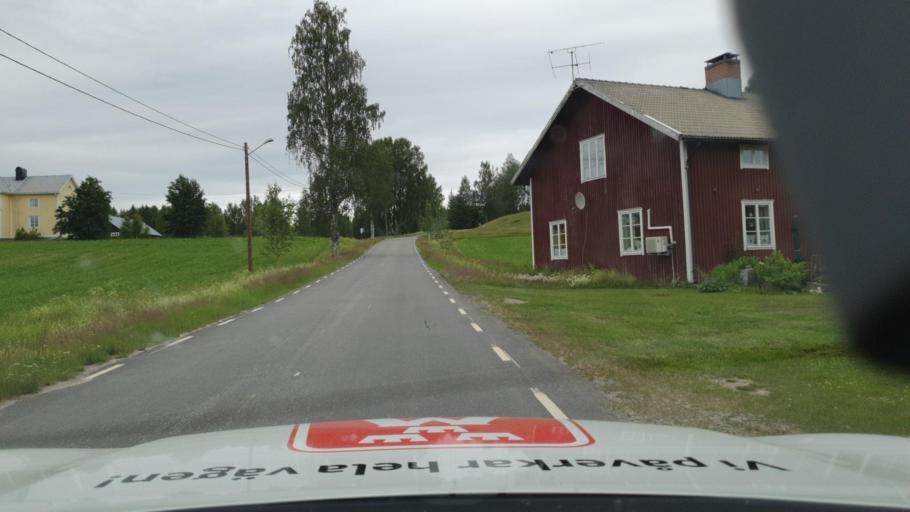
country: SE
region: Vaesterbotten
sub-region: Nordmalings Kommun
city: Nordmaling
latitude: 63.7298
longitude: 19.5063
